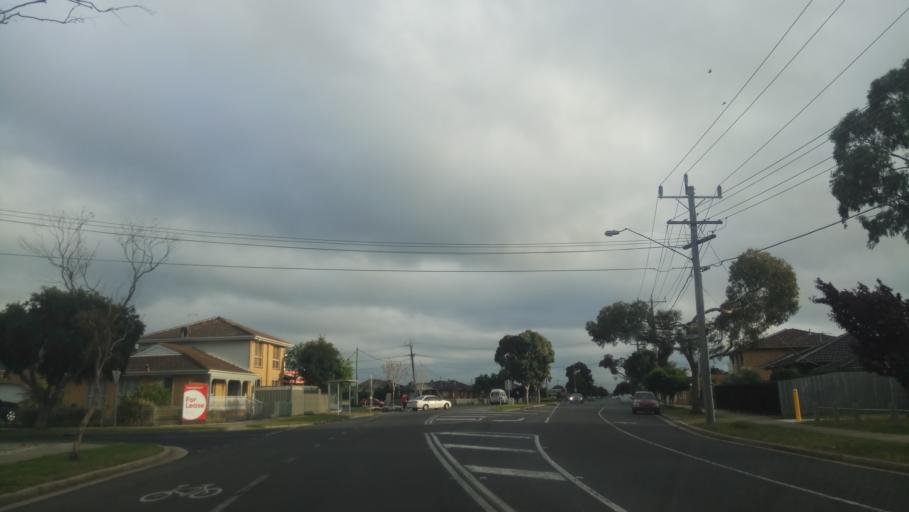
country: AU
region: Victoria
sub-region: Hobsons Bay
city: Altona Meadows
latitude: -37.8839
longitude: 144.7852
